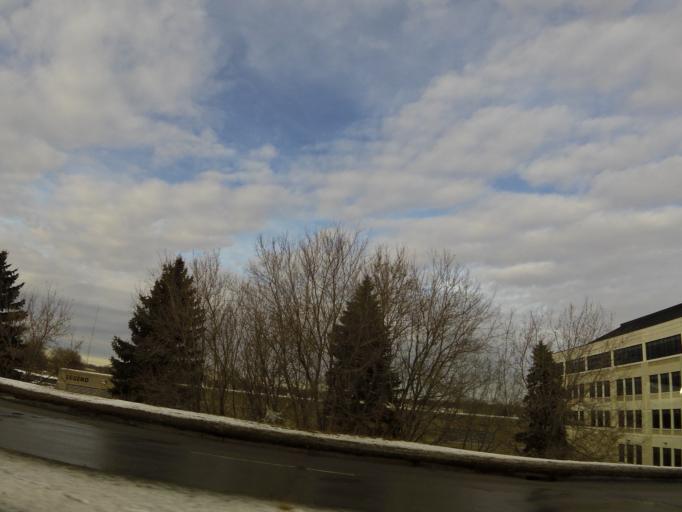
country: US
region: Minnesota
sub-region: Ramsey County
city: Saint Paul
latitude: 44.9607
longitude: -93.1029
